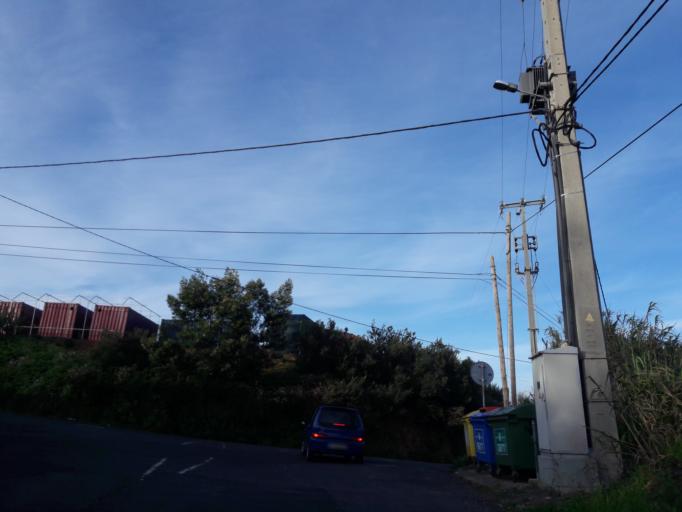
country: PT
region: Madeira
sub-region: Santa Cruz
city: Camacha
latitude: 32.6667
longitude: -16.8411
